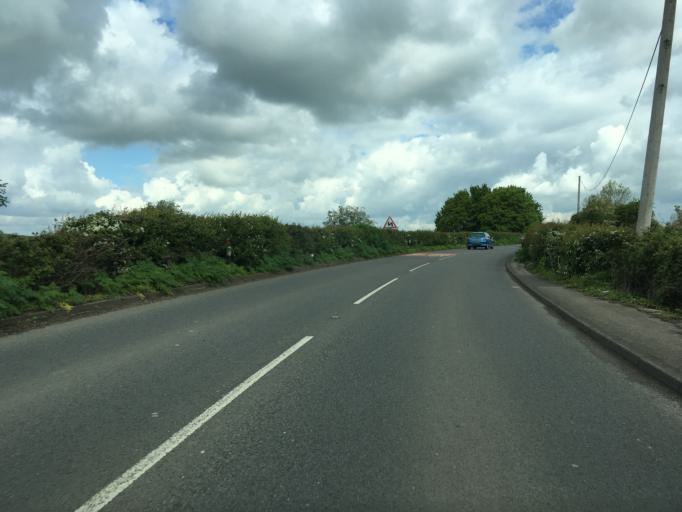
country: GB
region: England
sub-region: Gloucestershire
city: Stonehouse
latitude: 51.7695
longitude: -2.2826
